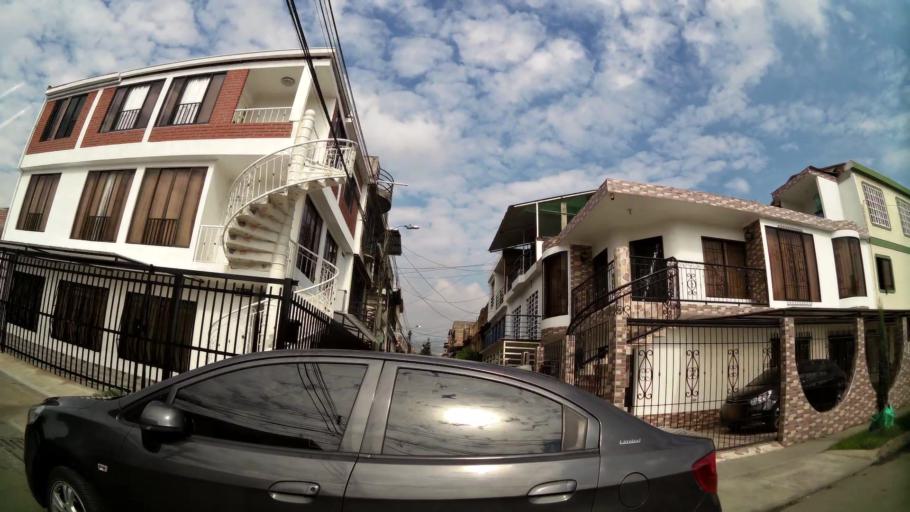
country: CO
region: Valle del Cauca
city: Cali
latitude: 3.4902
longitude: -76.4954
